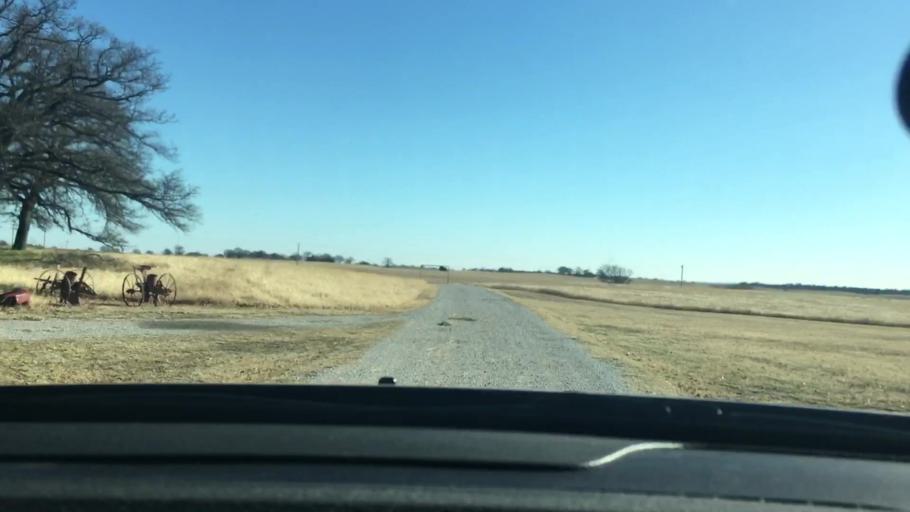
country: US
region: Oklahoma
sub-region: Love County
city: Marietta
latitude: 33.9093
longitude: -97.3547
